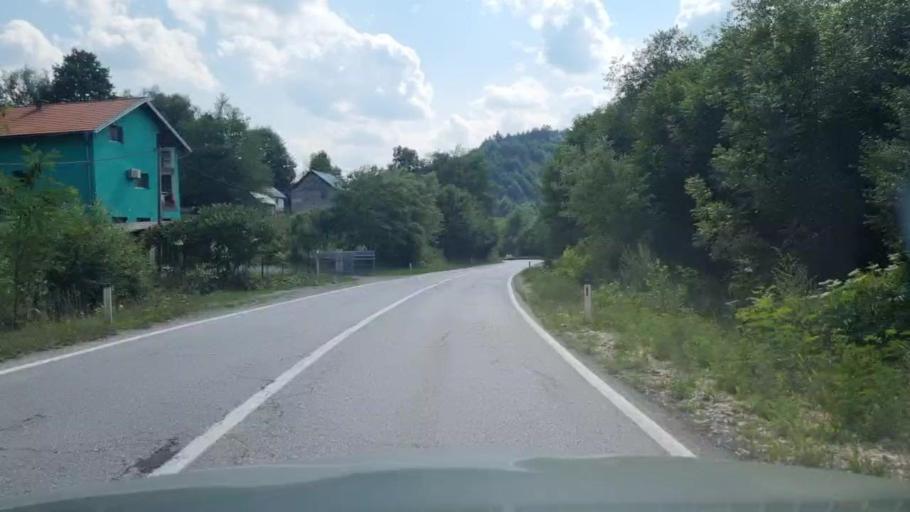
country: BA
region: Federation of Bosnia and Herzegovina
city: Olovo
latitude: 44.1579
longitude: 18.6381
